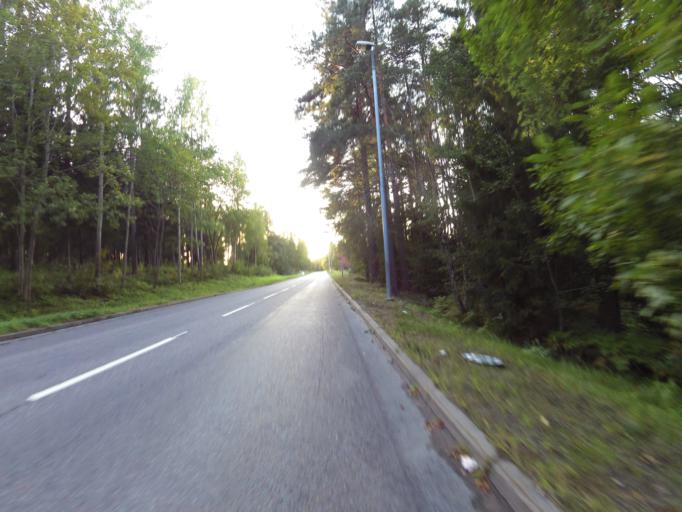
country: SE
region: Gaevleborg
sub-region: Gavle Kommun
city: Gavle
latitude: 60.6552
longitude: 17.1424
